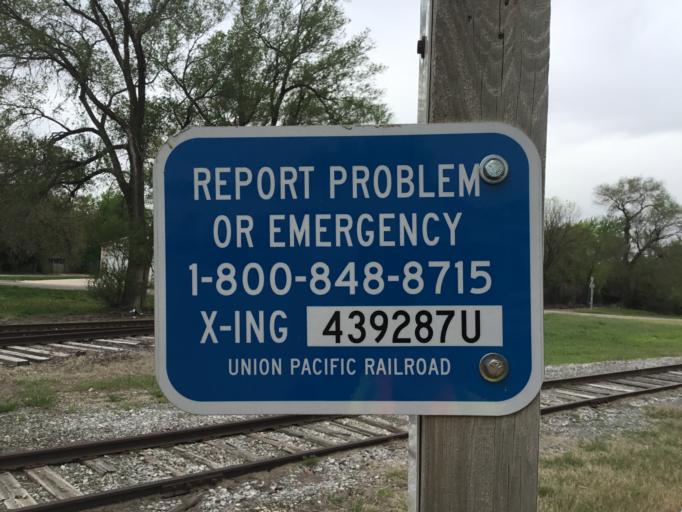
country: US
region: Kansas
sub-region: Butler County
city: El Dorado
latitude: 37.8227
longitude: -96.8505
